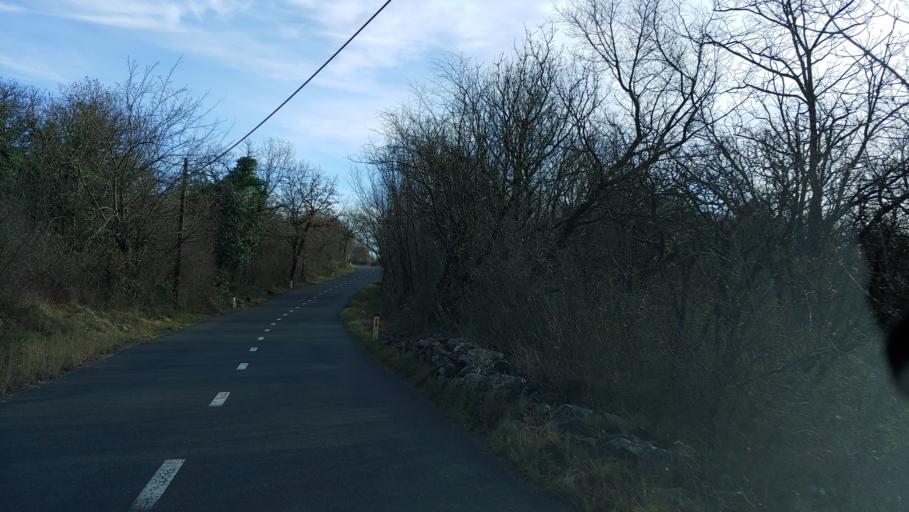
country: IT
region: Friuli Venezia Giulia
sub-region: Provincia di Trieste
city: Sistiana-Visogliano
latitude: 45.8110
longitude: 13.6803
